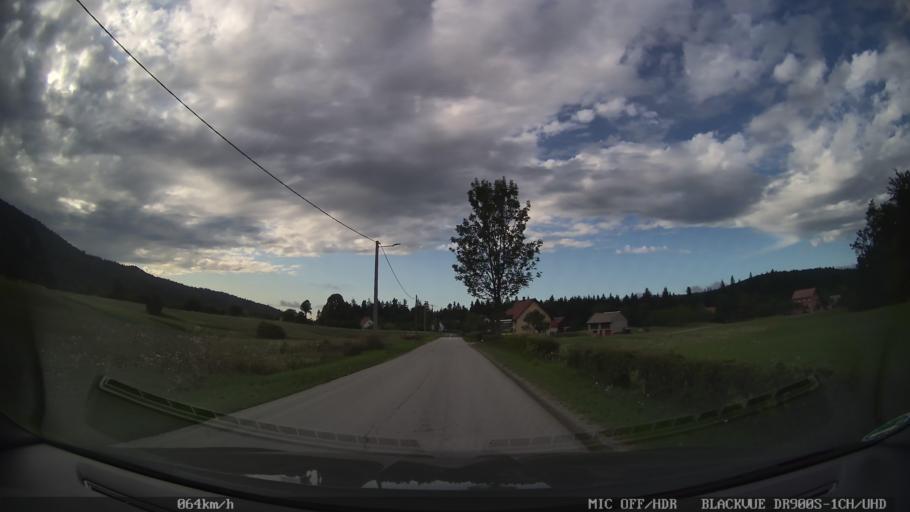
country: HR
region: Licko-Senjska
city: Jezerce
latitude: 44.9458
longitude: 15.5397
